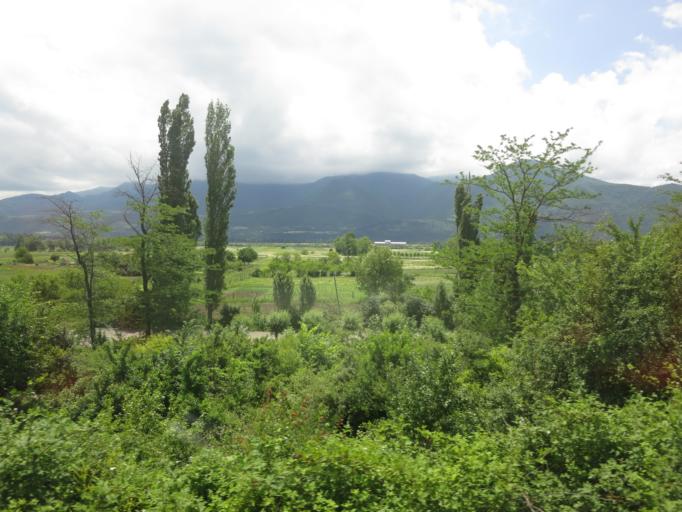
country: GE
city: Surami
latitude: 41.9871
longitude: 43.5314
